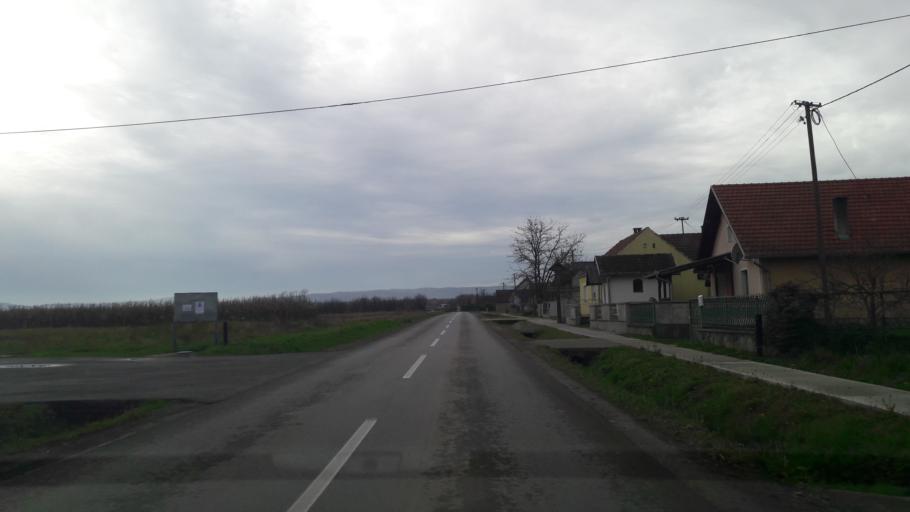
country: HR
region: Osjecko-Baranjska
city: Fericanci
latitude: 45.5275
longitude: 18.0167
